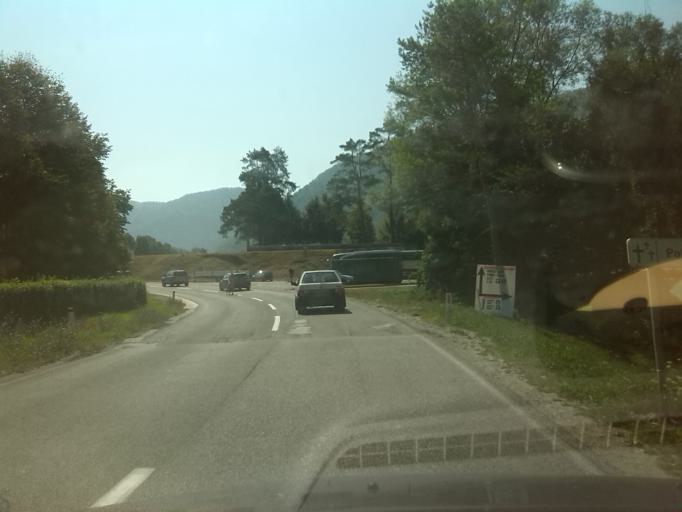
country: SI
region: Tolmin
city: Tolmin
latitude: 46.1814
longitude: 13.7251
